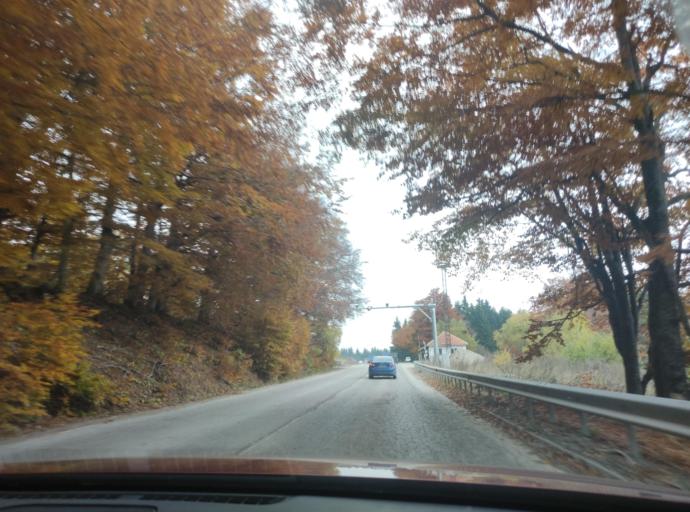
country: BG
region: Montana
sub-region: Obshtina Berkovitsa
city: Berkovitsa
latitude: 43.1202
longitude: 23.1224
